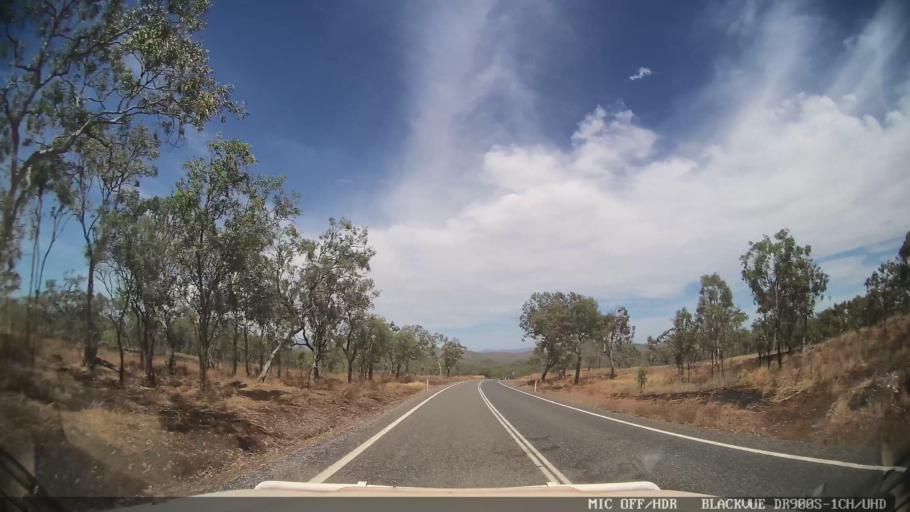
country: AU
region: Queensland
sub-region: Cook
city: Cooktown
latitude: -16.0201
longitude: 144.8118
